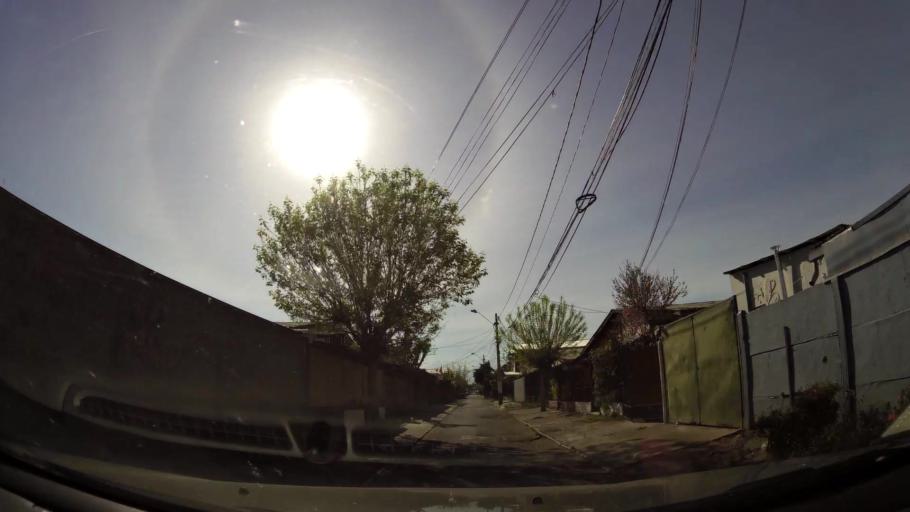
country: CL
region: Santiago Metropolitan
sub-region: Provincia de Cordillera
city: Puente Alto
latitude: -33.6083
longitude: -70.5990
